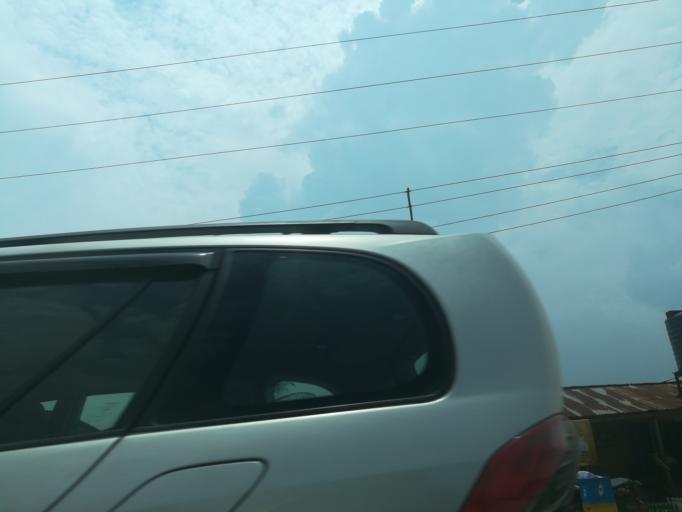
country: NG
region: Lagos
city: Ikorodu
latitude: 6.5971
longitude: 3.5886
